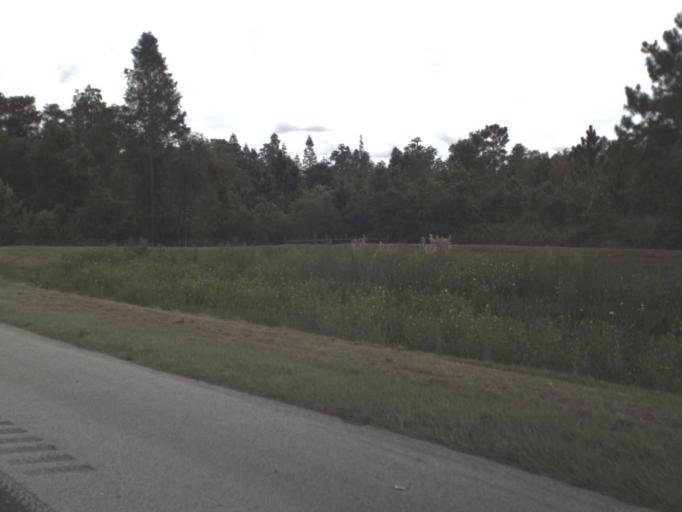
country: US
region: Florida
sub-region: Polk County
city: Lake Alfred
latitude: 28.1890
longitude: -81.7261
